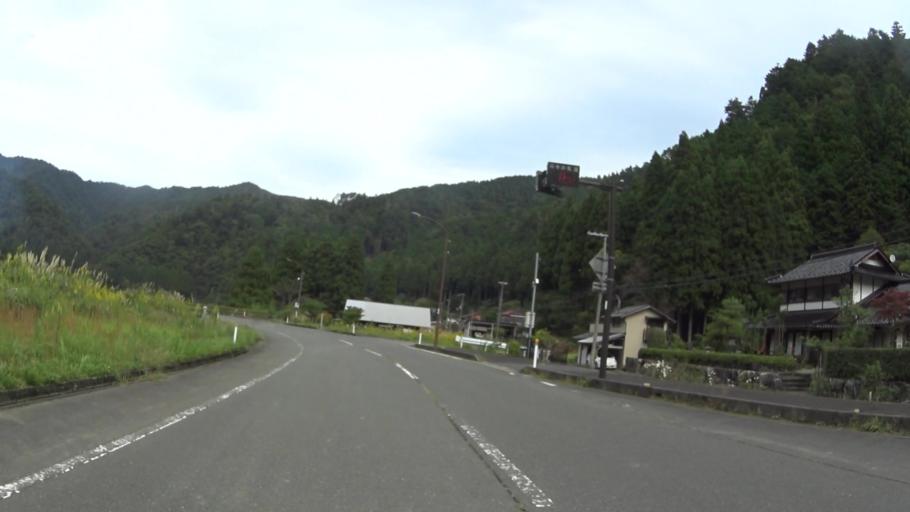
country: JP
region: Fukui
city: Obama
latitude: 35.3235
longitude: 135.6777
